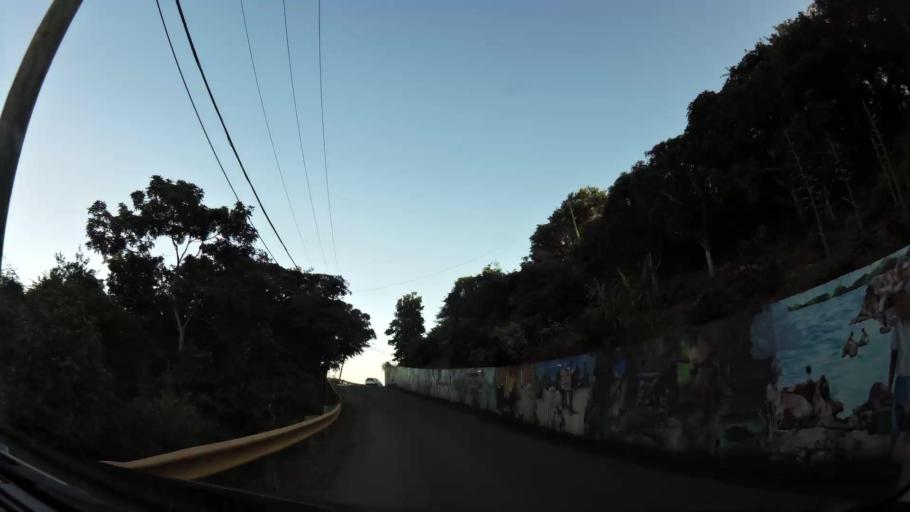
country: VG
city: Road Town
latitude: 18.4415
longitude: -64.6255
